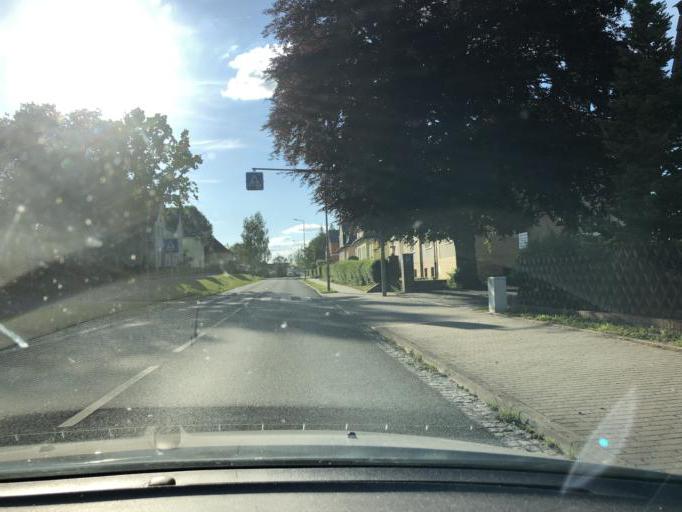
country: DE
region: Thuringia
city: Lodla
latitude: 51.0104
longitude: 12.3816
